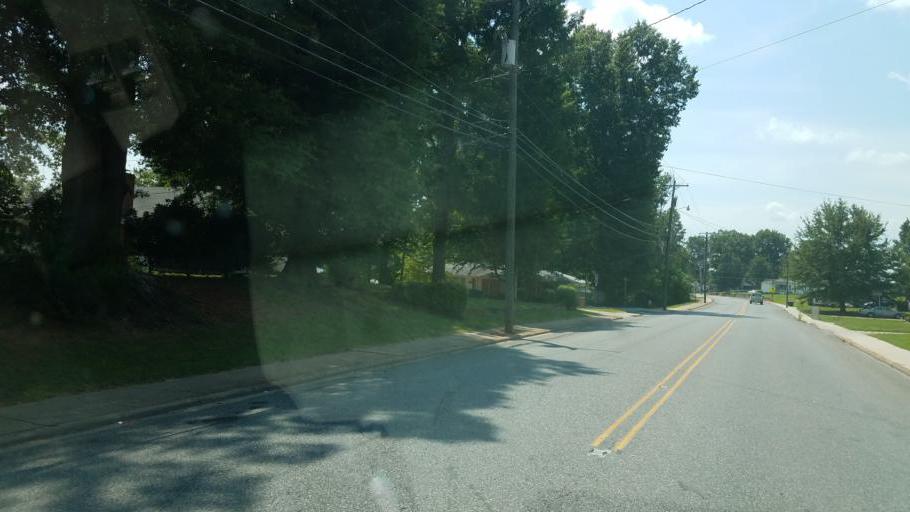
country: US
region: North Carolina
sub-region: Gaston County
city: Cherryville
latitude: 35.3728
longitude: -81.3774
